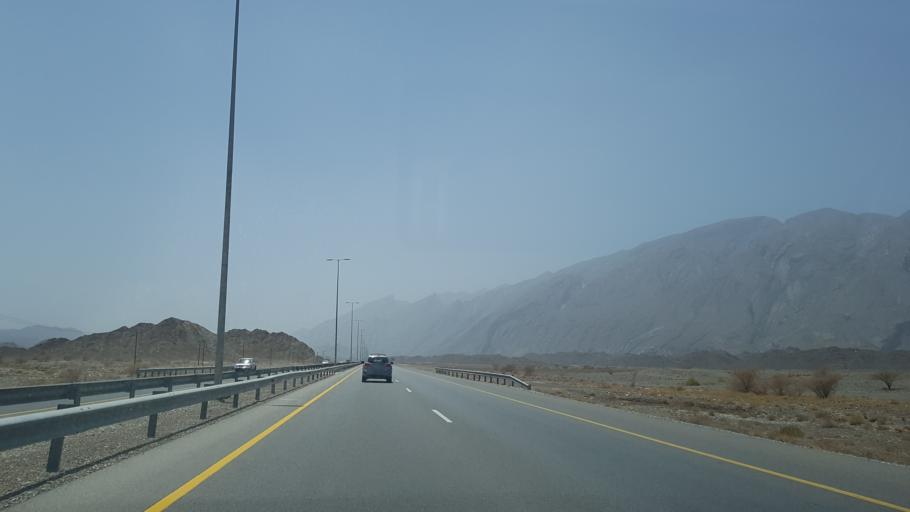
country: OM
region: Muhafazat ad Dakhiliyah
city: Sufalat Sama'il
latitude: 23.2416
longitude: 57.9140
